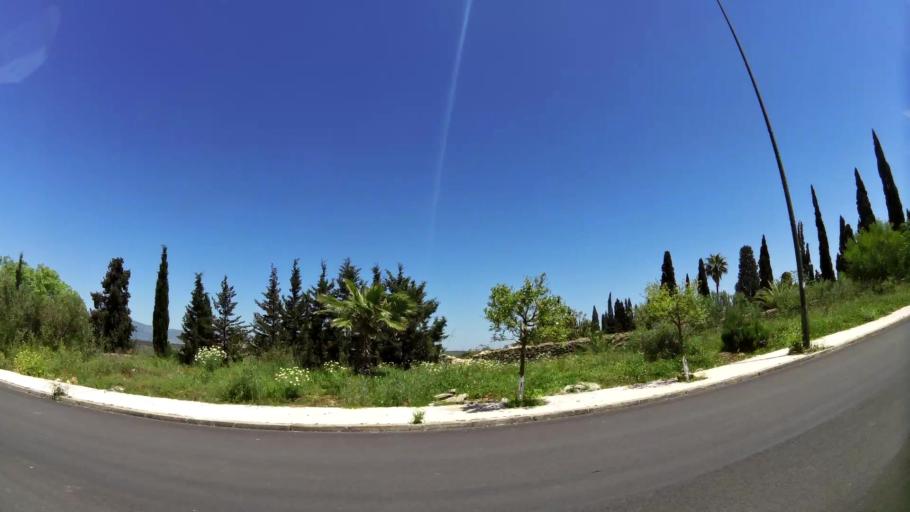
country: MA
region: Meknes-Tafilalet
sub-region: Meknes
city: Meknes
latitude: 33.9088
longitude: -5.5492
